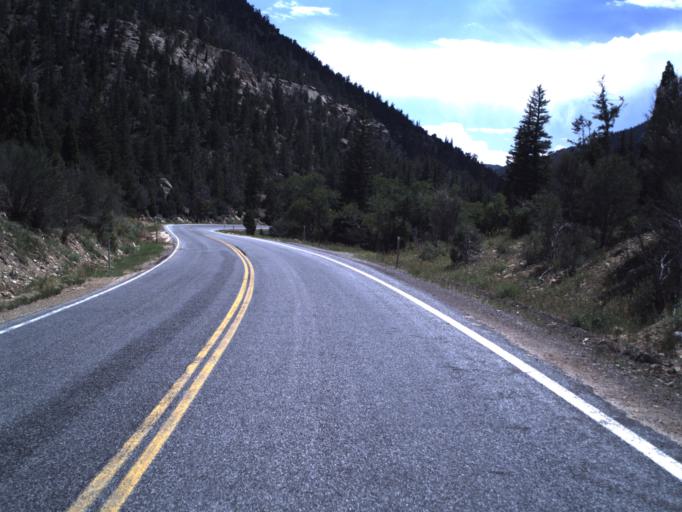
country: US
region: Utah
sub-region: Emery County
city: Huntington
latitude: 39.4352
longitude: -111.1318
